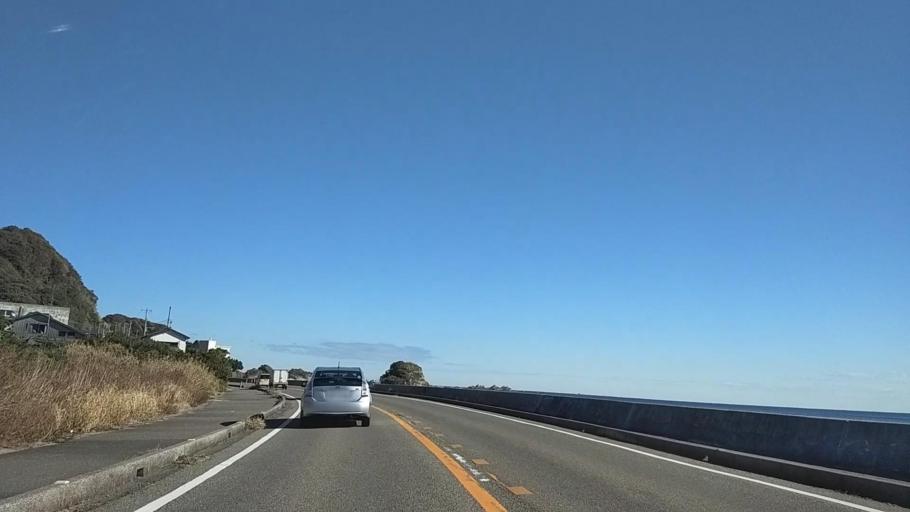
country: JP
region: Chiba
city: Kawaguchi
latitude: 35.0735
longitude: 140.0891
